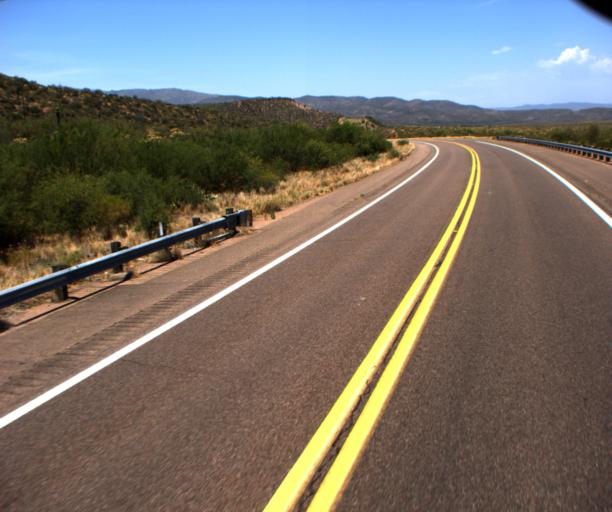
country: US
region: Arizona
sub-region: Gila County
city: Tonto Basin
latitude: 33.9332
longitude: -111.3142
